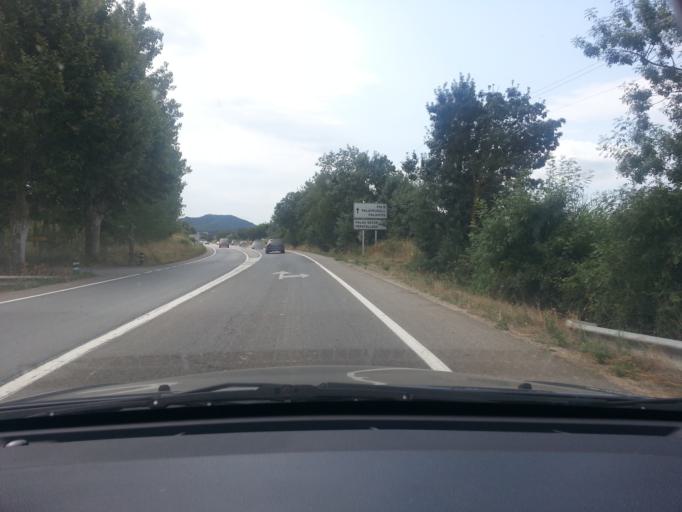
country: ES
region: Catalonia
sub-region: Provincia de Girona
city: Pals
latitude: 41.9957
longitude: 3.1493
